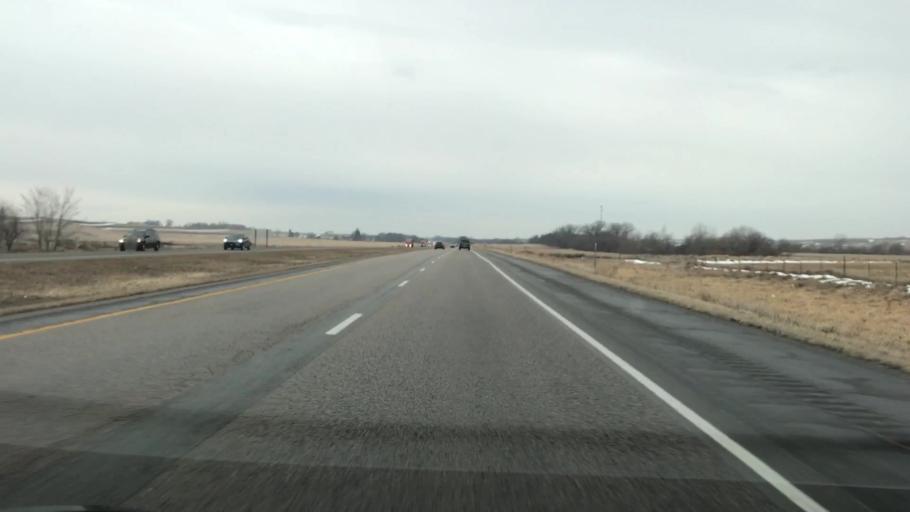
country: US
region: Iowa
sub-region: Pottawattamie County
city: Oakland
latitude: 41.4236
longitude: -95.6373
